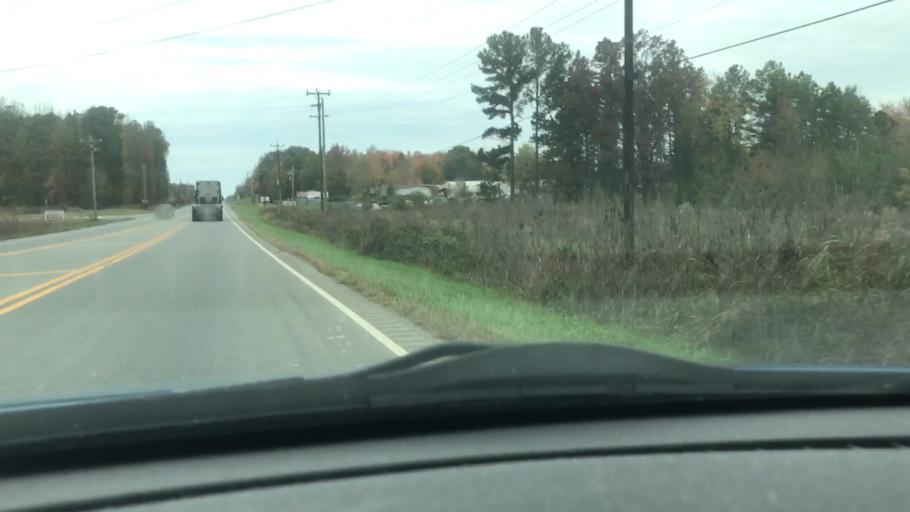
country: US
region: North Carolina
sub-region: Davidson County
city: Thomasville
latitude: 35.7804
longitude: -80.1229
